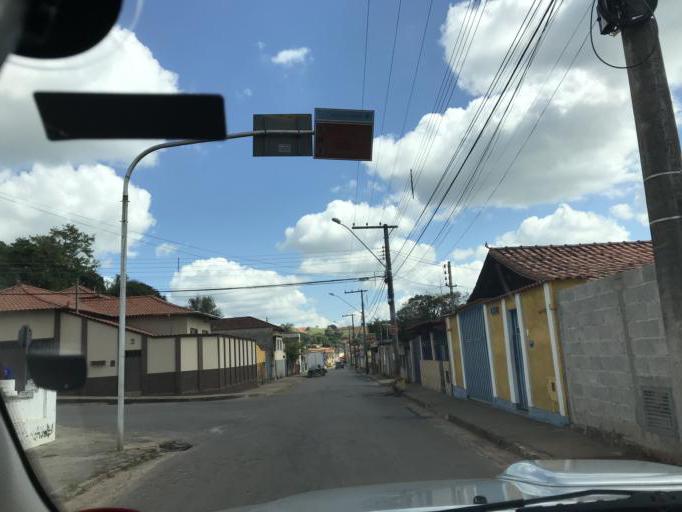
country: BR
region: Minas Gerais
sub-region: Campanha
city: Campanha
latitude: -21.8328
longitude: -45.4043
